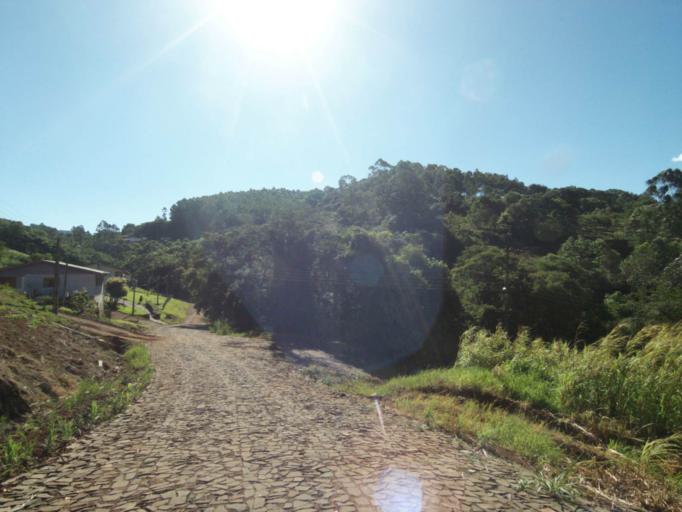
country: BR
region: Parana
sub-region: Ampere
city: Ampere
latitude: -26.1693
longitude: -53.3682
